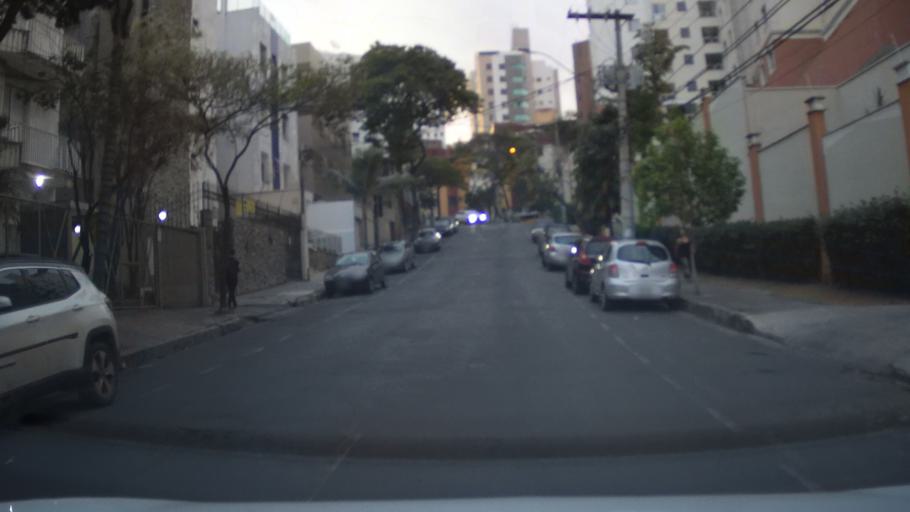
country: BR
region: Minas Gerais
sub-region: Belo Horizonte
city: Belo Horizonte
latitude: -19.8926
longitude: -43.9302
